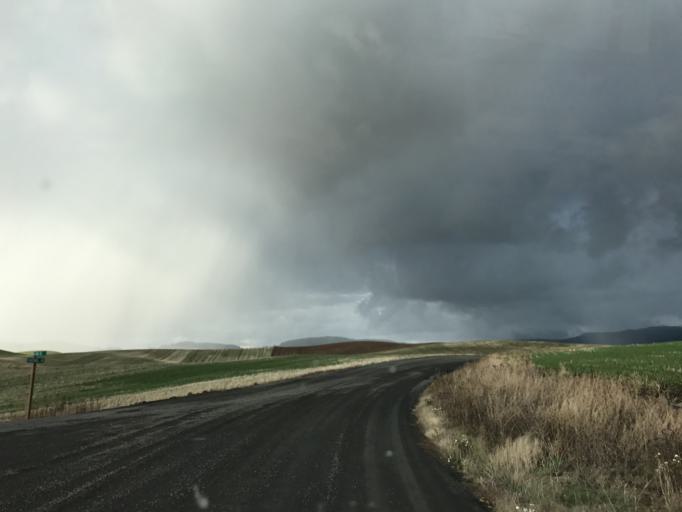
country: US
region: Idaho
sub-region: Latah County
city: Moscow
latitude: 46.7657
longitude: -116.9912
